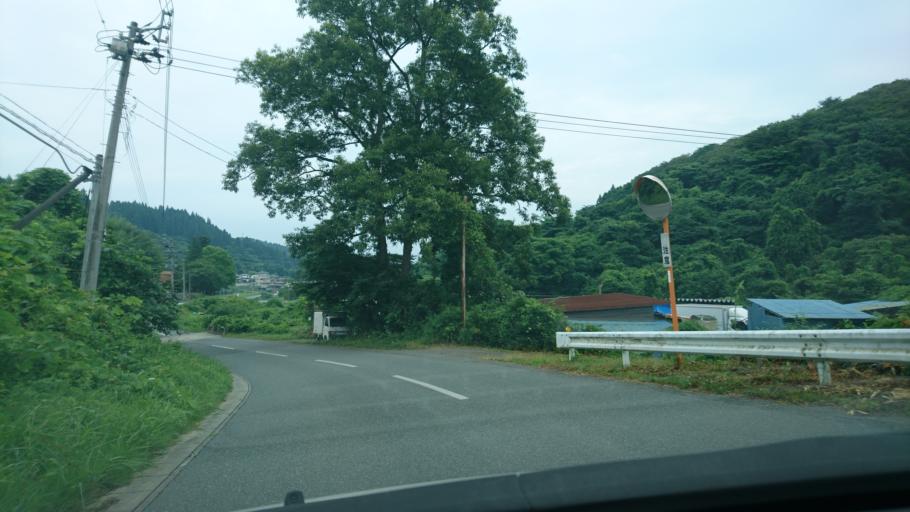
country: JP
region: Iwate
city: Ichinoseki
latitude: 38.9049
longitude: 141.1180
